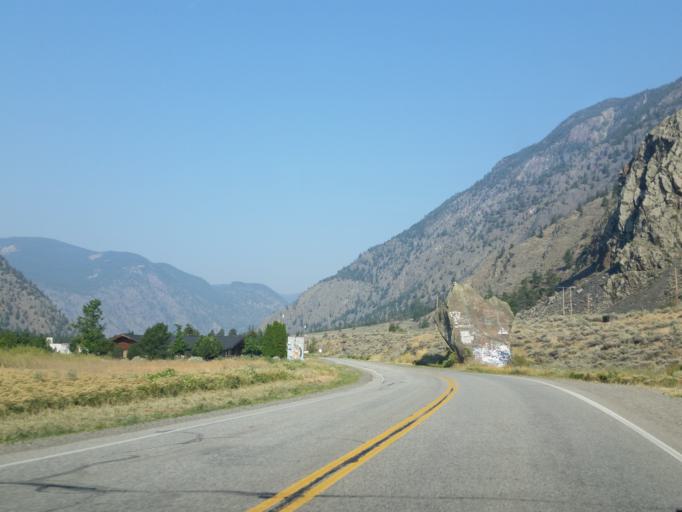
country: CA
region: British Columbia
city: Oliver
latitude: 49.2167
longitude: -119.9135
